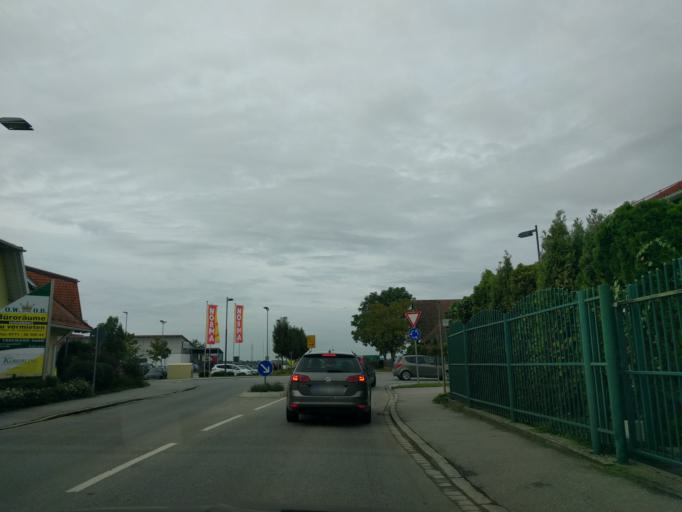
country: DE
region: Bavaria
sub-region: Lower Bavaria
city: Plattling
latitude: 48.7727
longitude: 12.8577
